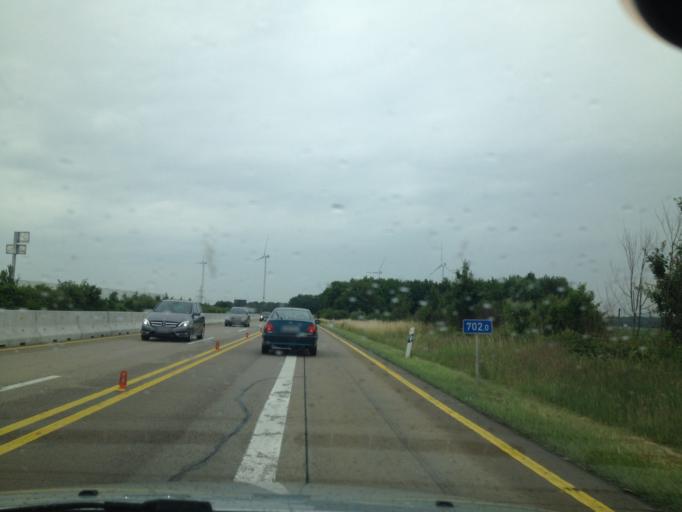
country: DE
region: Bavaria
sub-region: Regierungsbezirk Mittelfranken
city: Uffenheim
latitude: 49.5177
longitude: 10.1964
